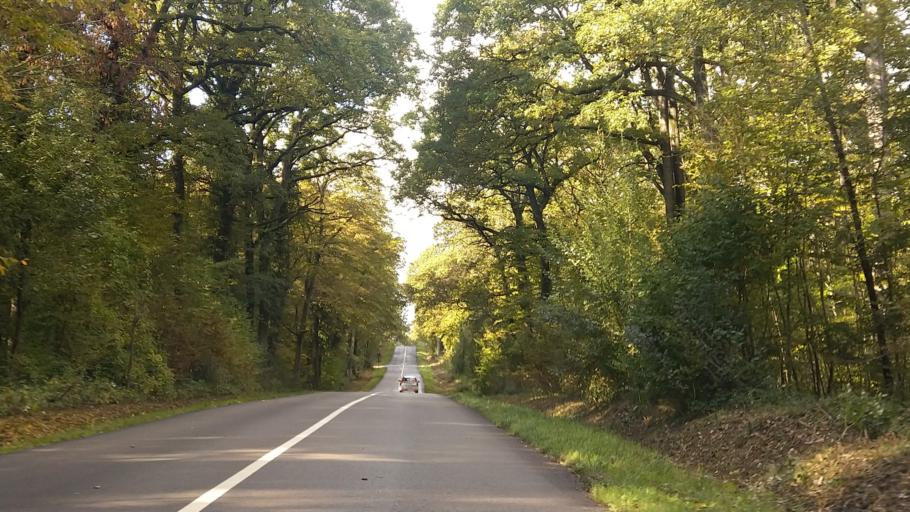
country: FR
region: Ile-de-France
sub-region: Departement du Val-d'Oise
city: Baillet-en-France
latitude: 49.0792
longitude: 2.2682
